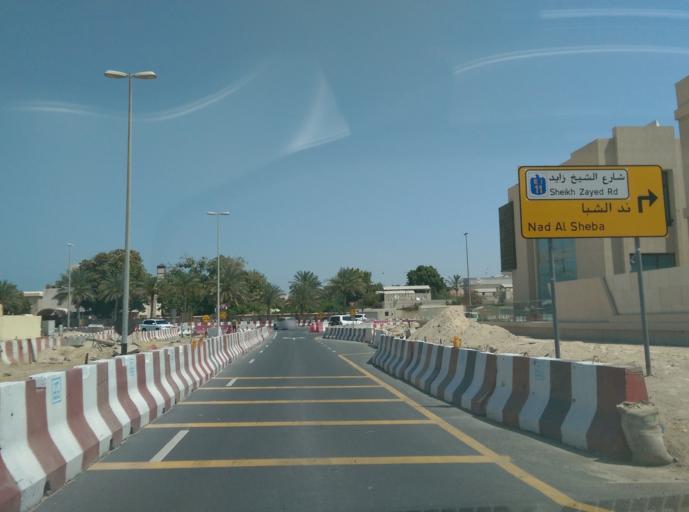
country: AE
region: Dubai
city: Dubai
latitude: 25.1904
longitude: 55.2360
